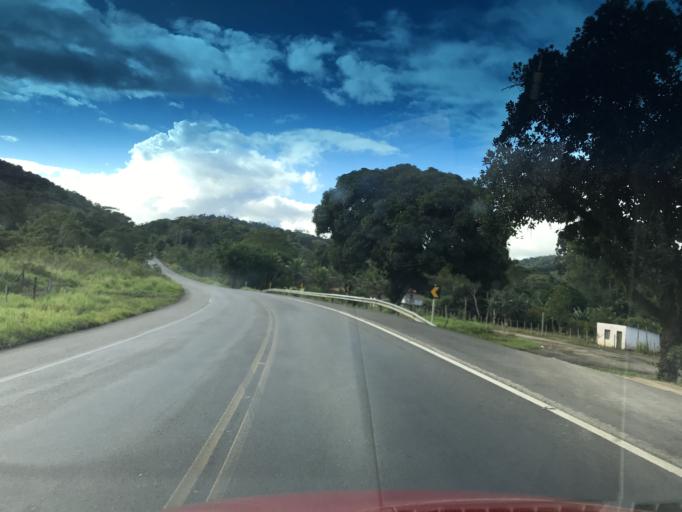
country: BR
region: Bahia
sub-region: Ibirapitanga
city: Ibirapitanga
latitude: -14.1981
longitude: -39.3137
